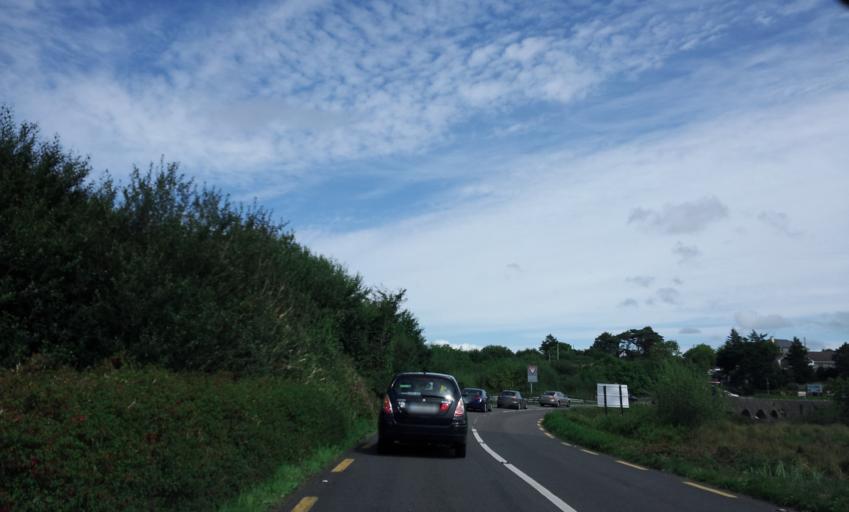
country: IE
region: Munster
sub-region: Ciarrai
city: Killorglin
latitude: 52.0679
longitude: -9.9052
